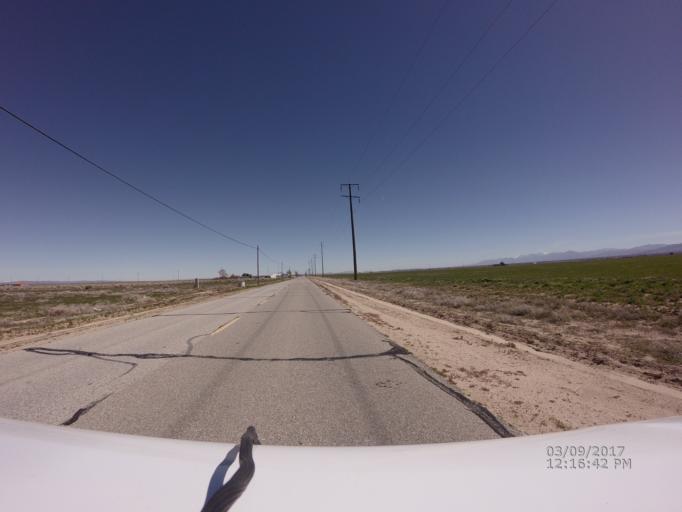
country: US
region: California
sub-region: Los Angeles County
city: Quartz Hill
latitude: 34.7330
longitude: -118.2598
